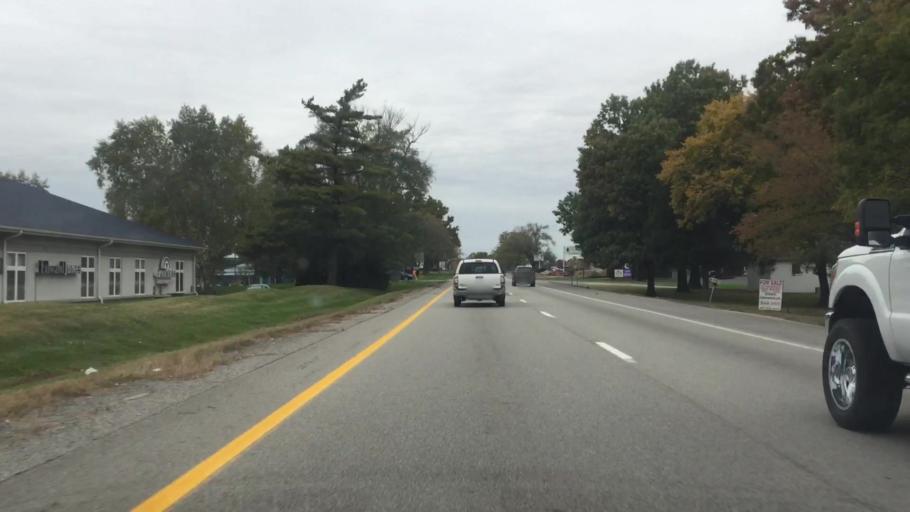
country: US
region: Missouri
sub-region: Jackson County
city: Raytown
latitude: 38.9810
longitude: -94.4545
